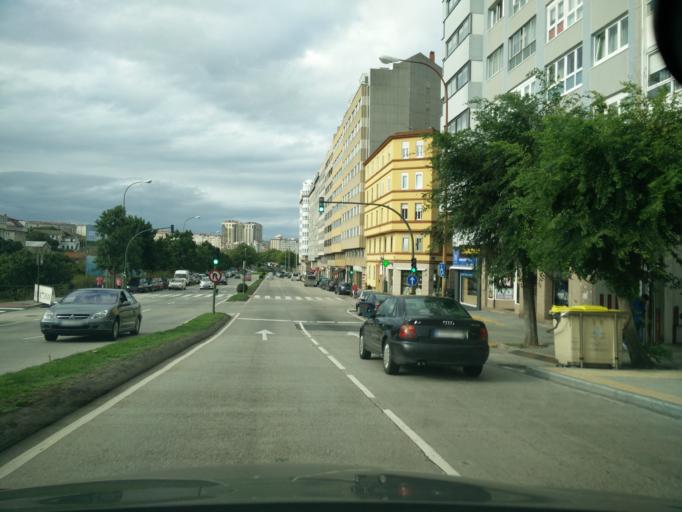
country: ES
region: Galicia
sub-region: Provincia da Coruna
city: A Coruna
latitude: 43.3659
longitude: -8.4246
